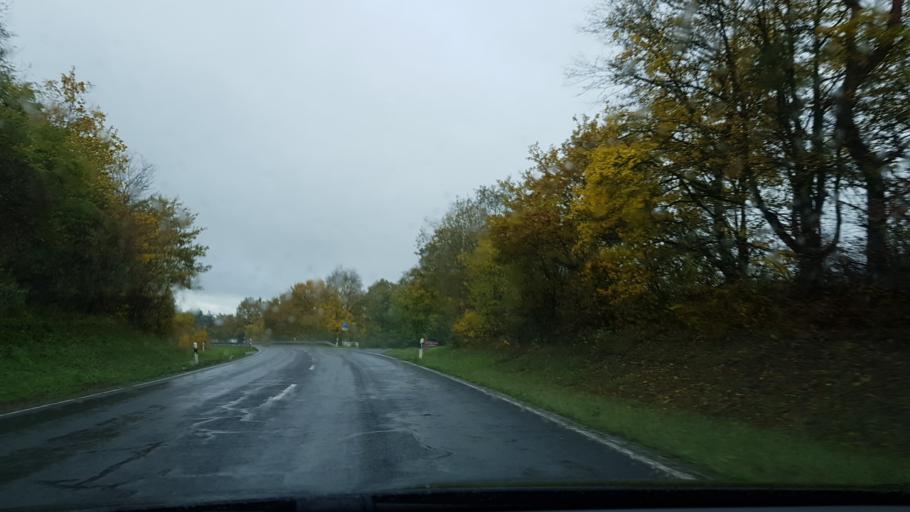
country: DE
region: Rheinland-Pfalz
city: Salmtal
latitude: 49.9445
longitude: 6.8460
